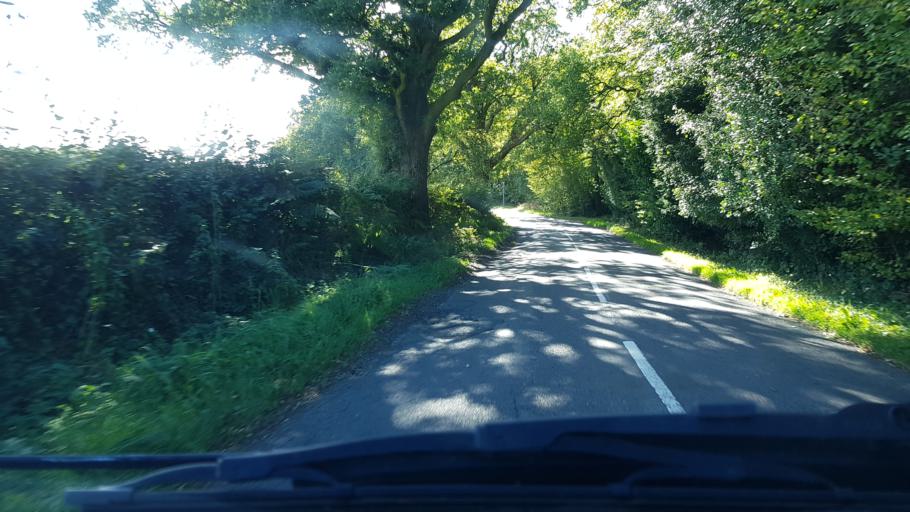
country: GB
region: England
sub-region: Surrey
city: Chiddingfold
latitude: 51.0864
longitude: -0.5779
